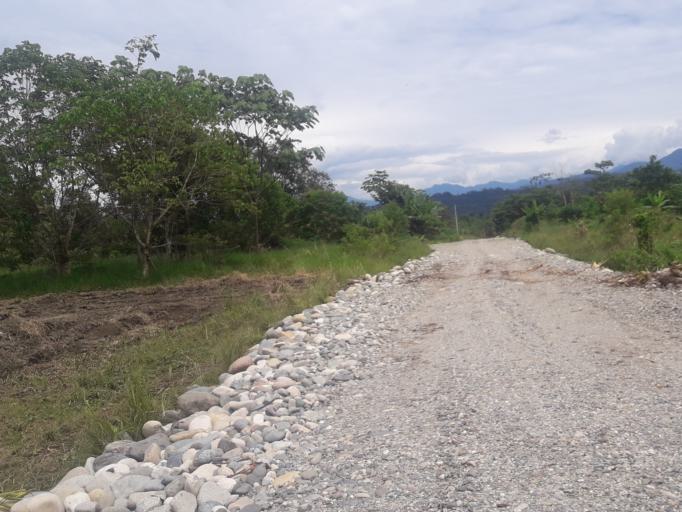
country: EC
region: Napo
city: Tena
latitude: -1.0609
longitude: -77.7941
